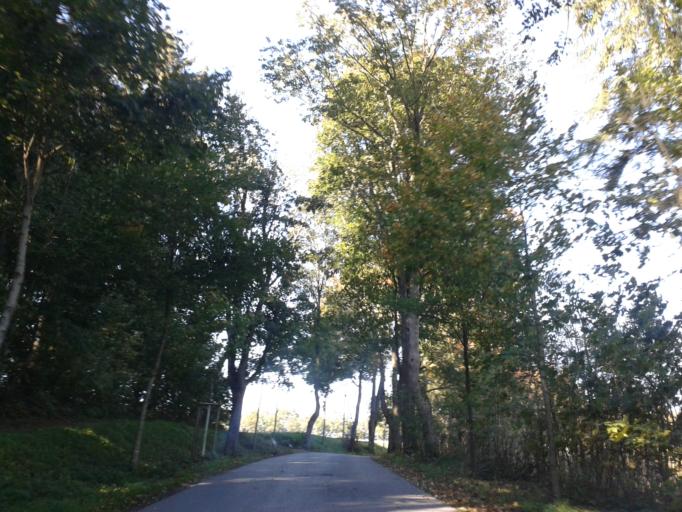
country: DE
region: North Rhine-Westphalia
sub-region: Regierungsbezirk Detmold
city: Paderborn
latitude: 51.6886
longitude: 8.7908
